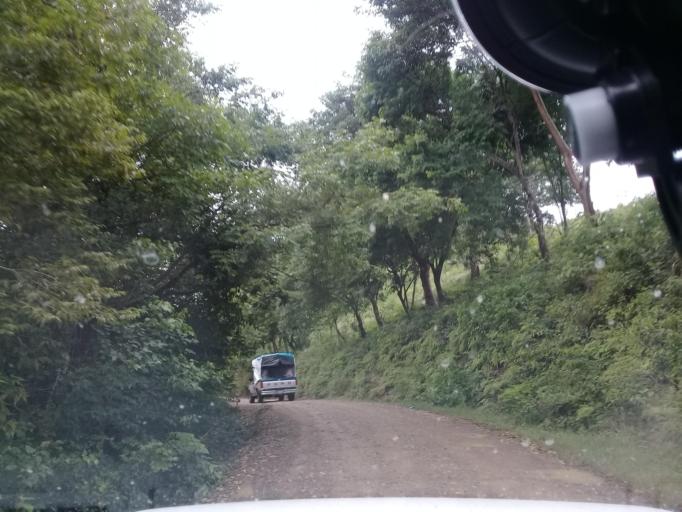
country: MX
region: Veracruz
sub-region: Chalma
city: San Pedro Coyutla
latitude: 21.2316
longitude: -98.4207
